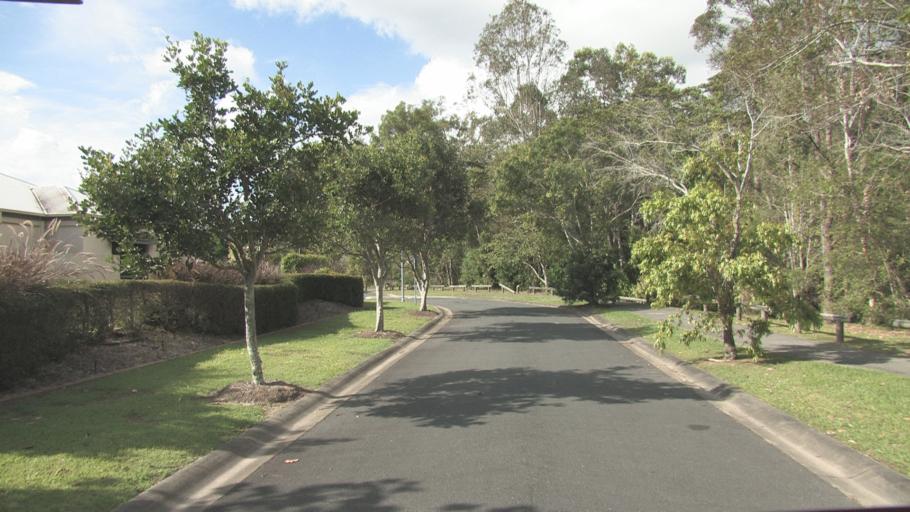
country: AU
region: Queensland
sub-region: Logan
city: Beenleigh
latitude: -27.6606
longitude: 153.2081
